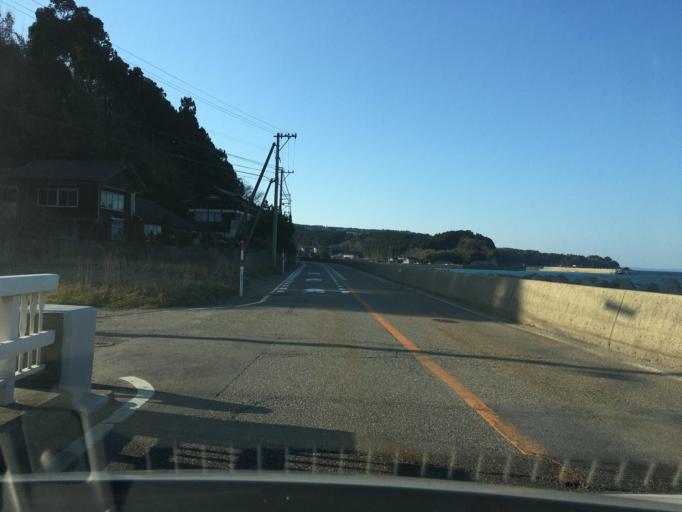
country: JP
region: Ishikawa
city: Nanao
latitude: 36.9724
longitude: 137.0527
